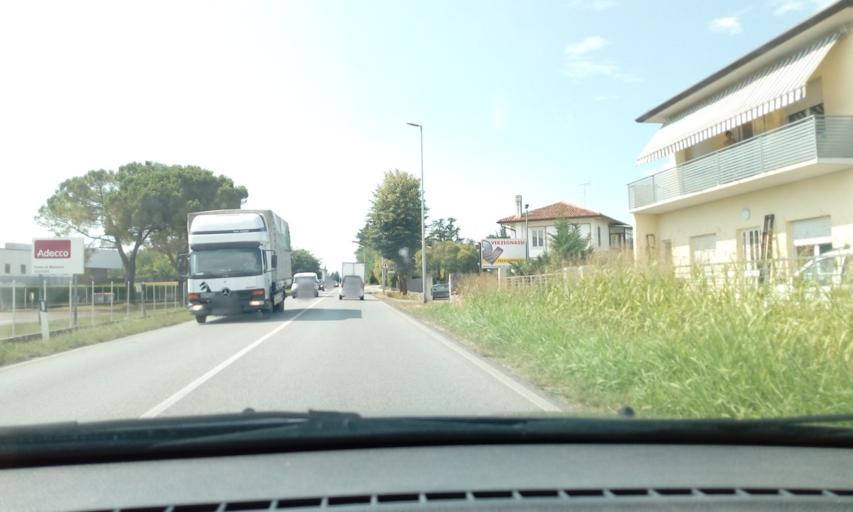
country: IT
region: Friuli Venezia Giulia
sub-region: Provincia di Udine
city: Manzano
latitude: 45.9847
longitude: 13.3756
